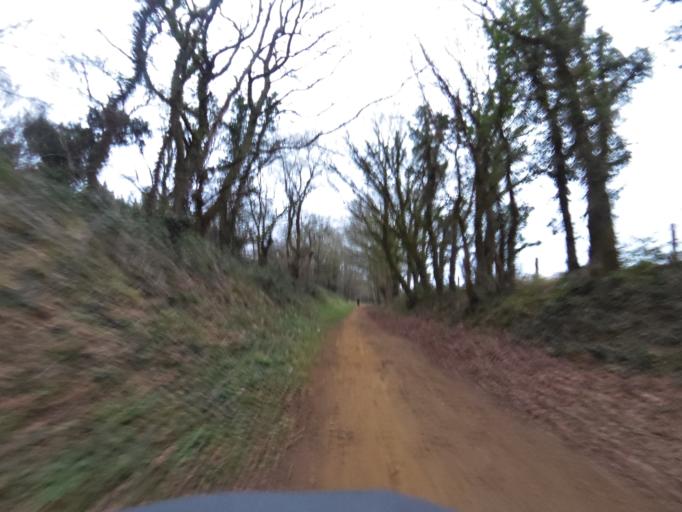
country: GB
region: England
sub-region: Norfolk
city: Horsford
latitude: 52.7040
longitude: 1.1926
